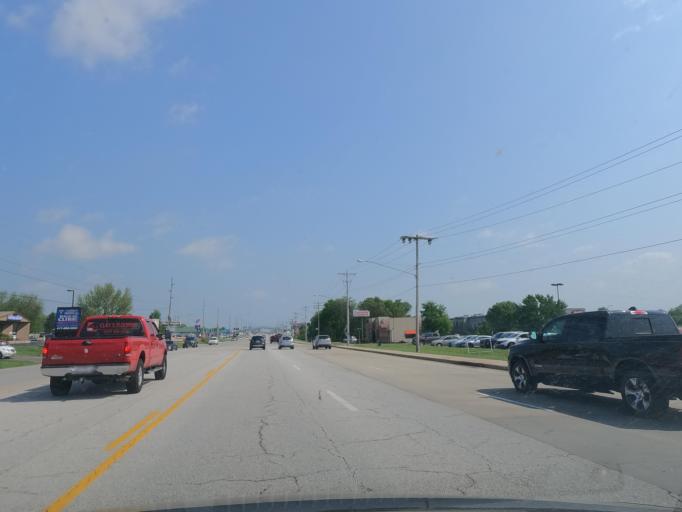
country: US
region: Missouri
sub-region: Greene County
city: Springfield
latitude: 37.1397
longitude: -93.2961
